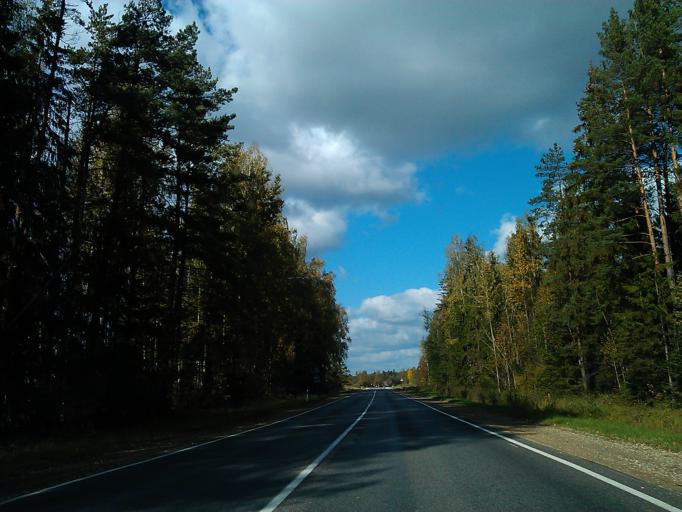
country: LV
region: Livani
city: Livani
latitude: 56.2456
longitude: 26.2103
